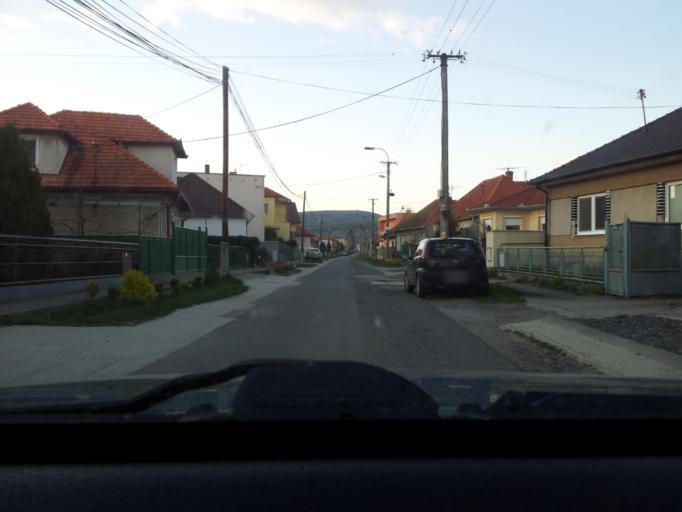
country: SK
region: Nitriansky
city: Levice
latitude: 48.2857
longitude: 18.6024
